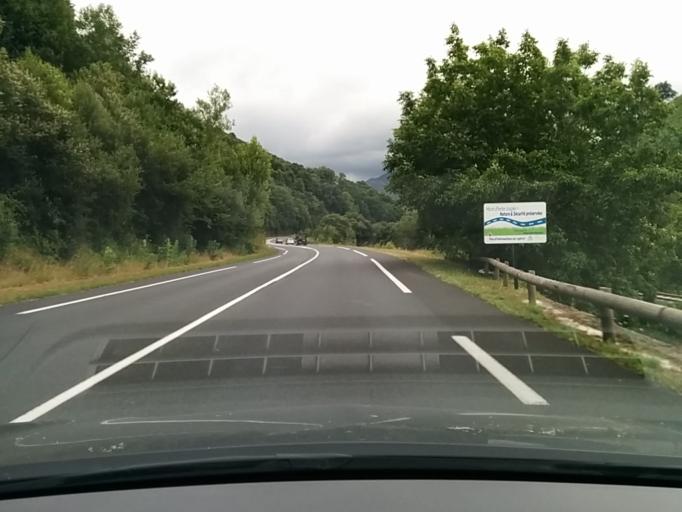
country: FR
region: Aquitaine
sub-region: Departement des Pyrenees-Atlantiques
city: Itxassou
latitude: 43.2992
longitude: -1.3500
